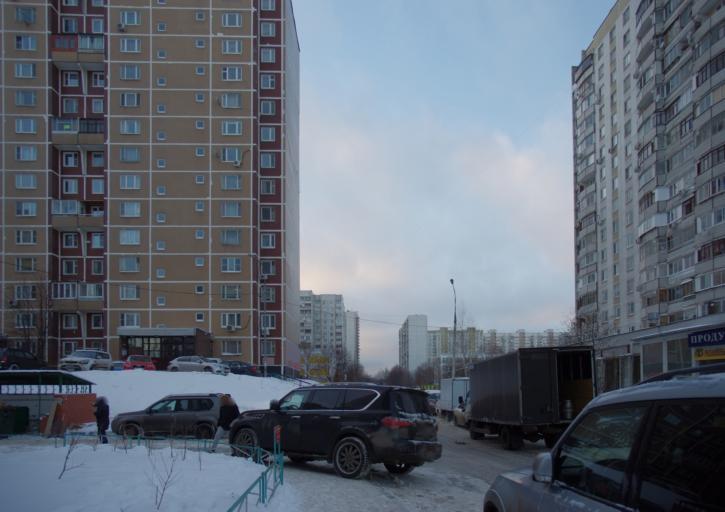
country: RU
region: Moscow
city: Tsaritsyno
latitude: 55.6402
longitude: 37.6639
